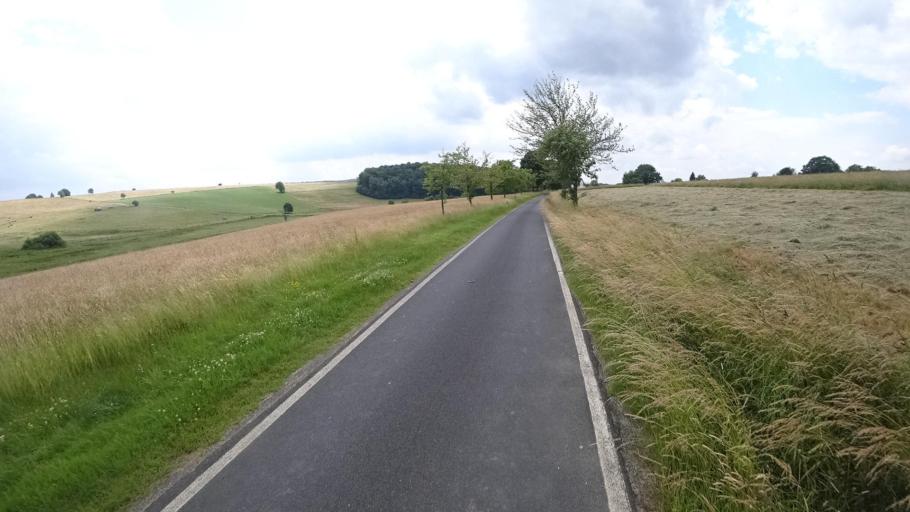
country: DE
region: Rheinland-Pfalz
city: Volkerzen
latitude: 50.7260
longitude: 7.6859
